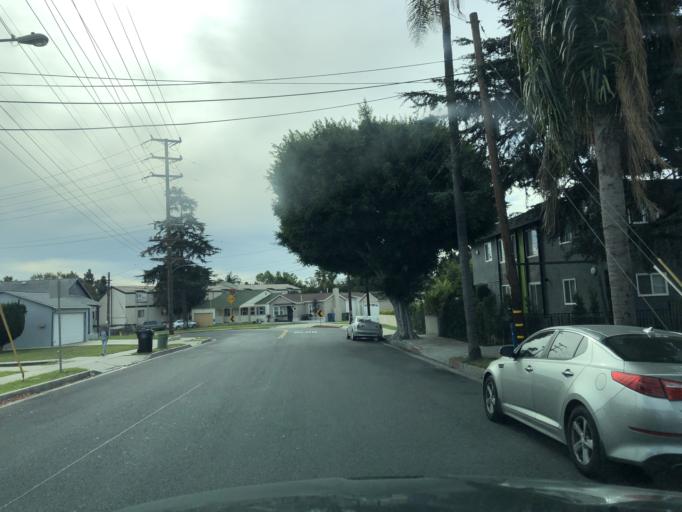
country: US
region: California
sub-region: Los Angeles County
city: Inglewood
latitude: 33.9751
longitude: -118.3668
